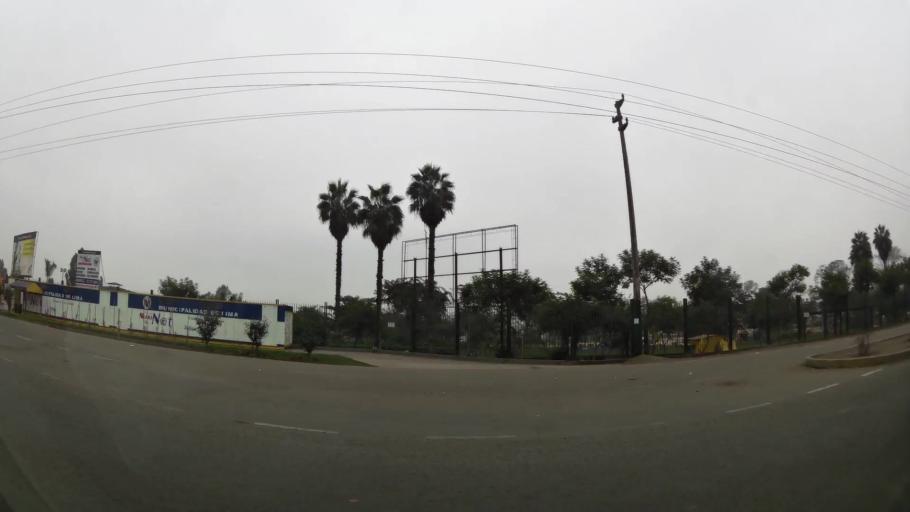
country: PE
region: Lima
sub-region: Lima
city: Urb. Santo Domingo
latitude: -11.8886
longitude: -77.0255
